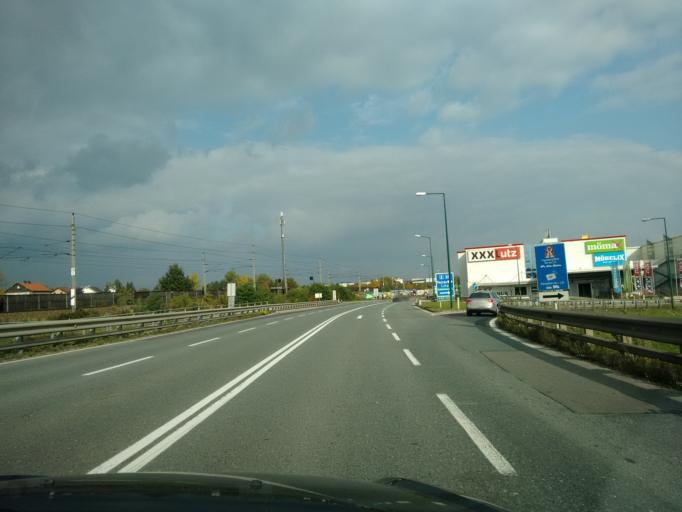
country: AT
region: Upper Austria
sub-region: Wels-Land
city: Gunskirchen
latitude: 48.1519
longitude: 13.9820
